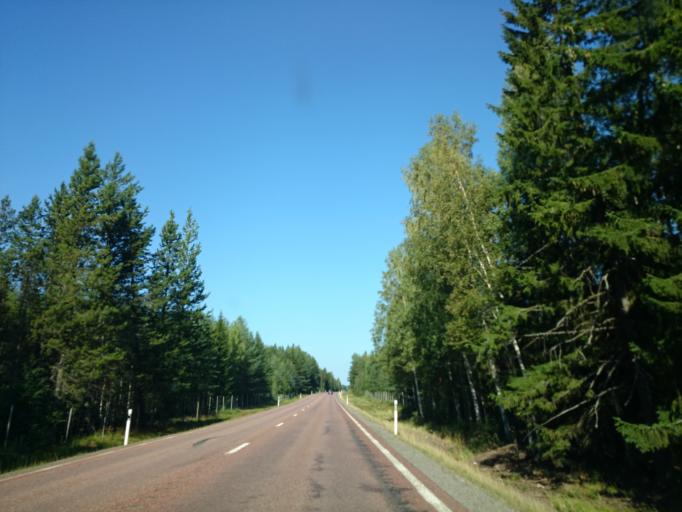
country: SE
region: Gaevleborg
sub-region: Hudiksvalls Kommun
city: Delsbo
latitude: 61.7914
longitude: 16.5905
